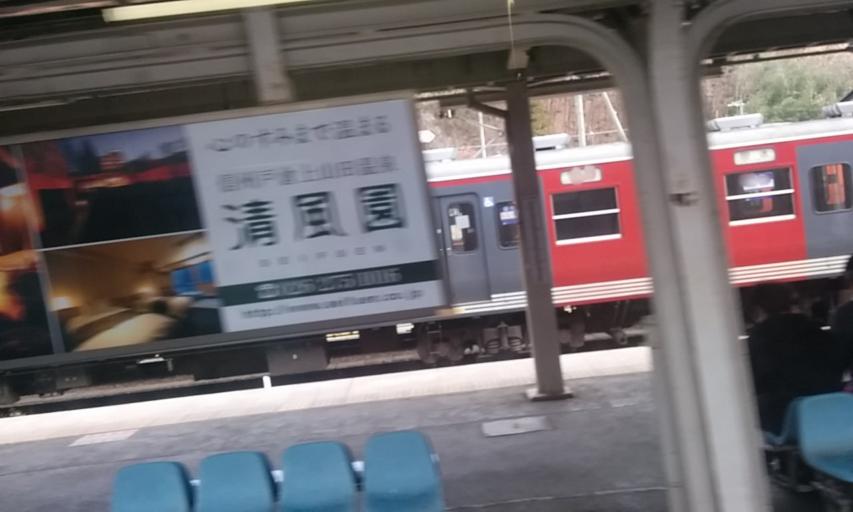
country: JP
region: Nagano
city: Ueda
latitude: 36.4922
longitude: 138.1534
